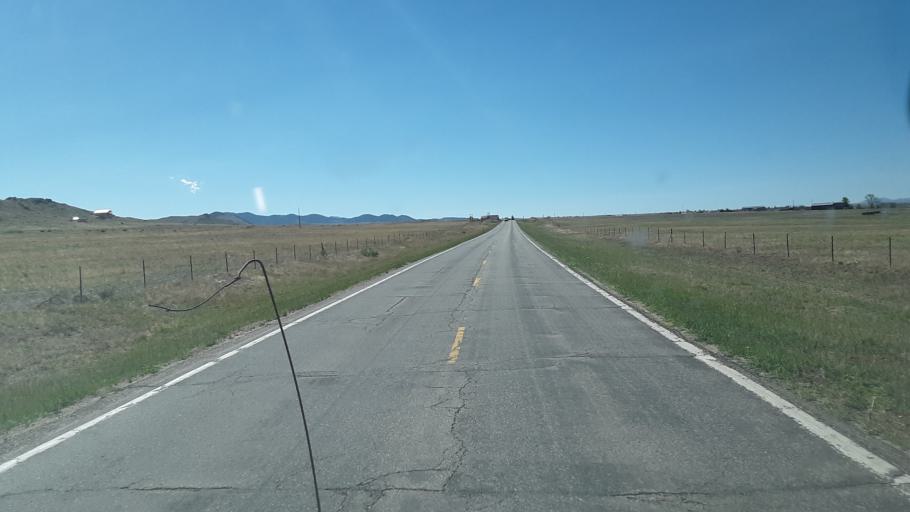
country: US
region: Colorado
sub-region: Custer County
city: Westcliffe
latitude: 38.1676
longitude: -105.4894
